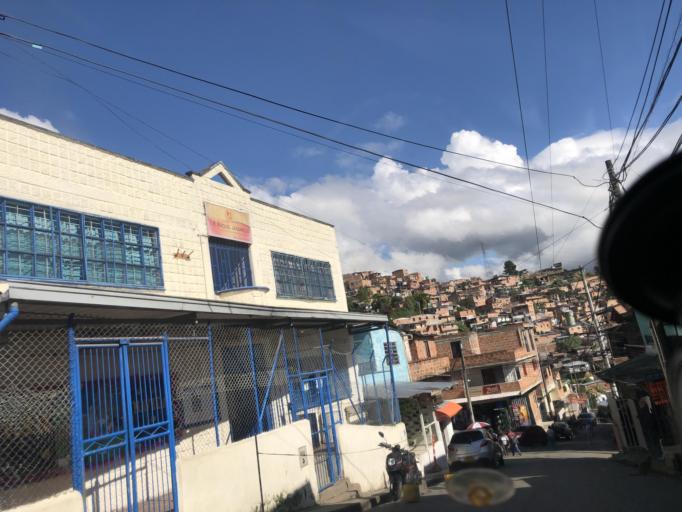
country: CO
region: Antioquia
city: Bello
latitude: 6.3145
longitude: -75.5785
